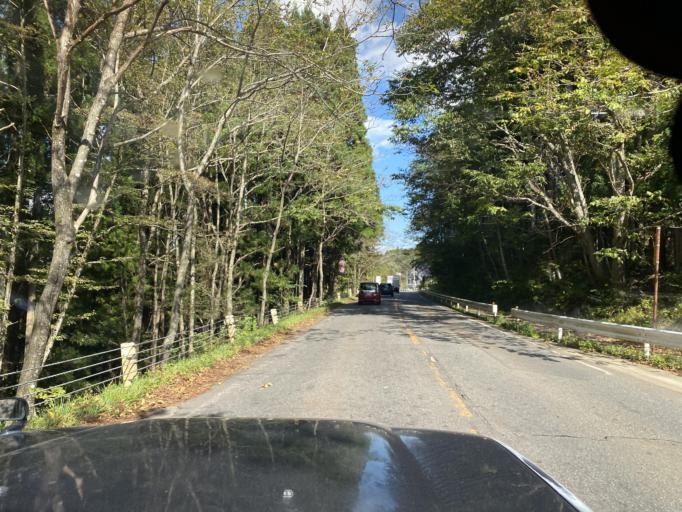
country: JP
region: Nagano
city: Omachi
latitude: 36.5935
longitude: 137.8447
